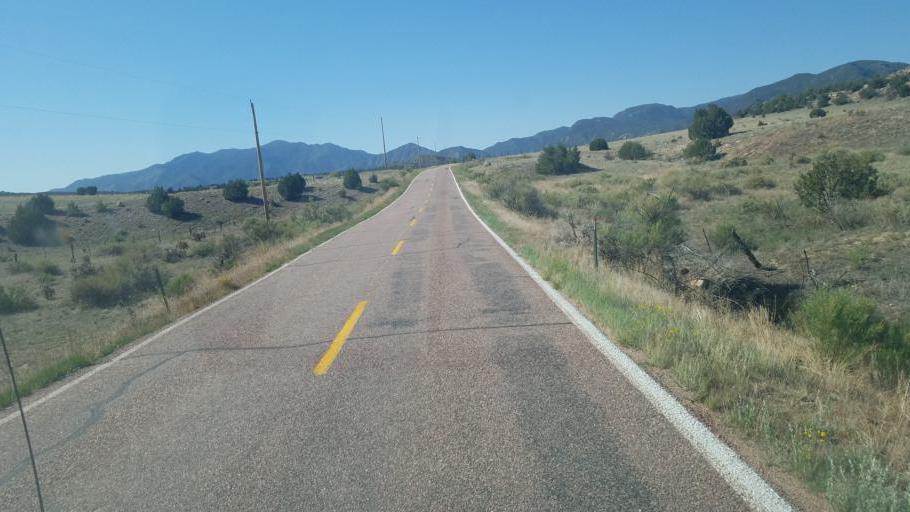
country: US
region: Colorado
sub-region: Fremont County
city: Canon City
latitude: 38.4682
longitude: -105.3777
